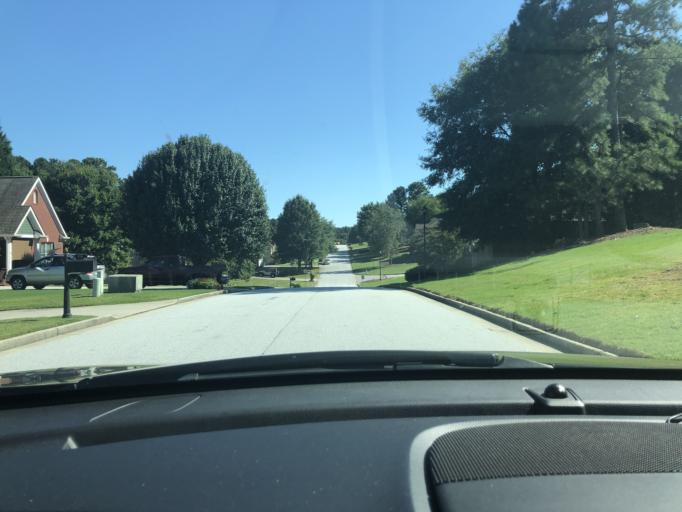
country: US
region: Georgia
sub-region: Gwinnett County
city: Grayson
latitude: 33.9096
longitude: -83.9212
